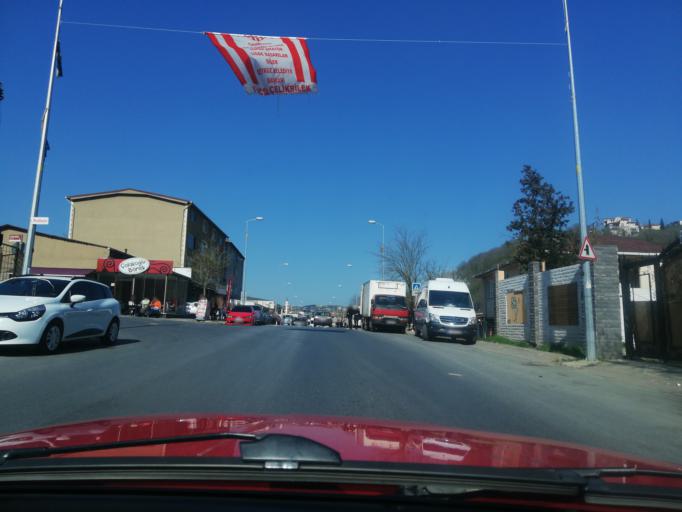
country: TR
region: Istanbul
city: Umraniye
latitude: 41.0875
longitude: 29.1374
